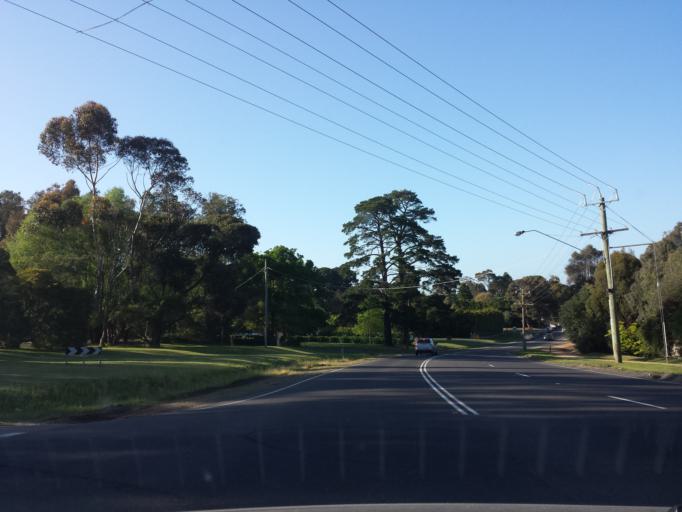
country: AU
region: Victoria
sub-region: Casey
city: Berwick
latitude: -38.0175
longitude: 145.3462
